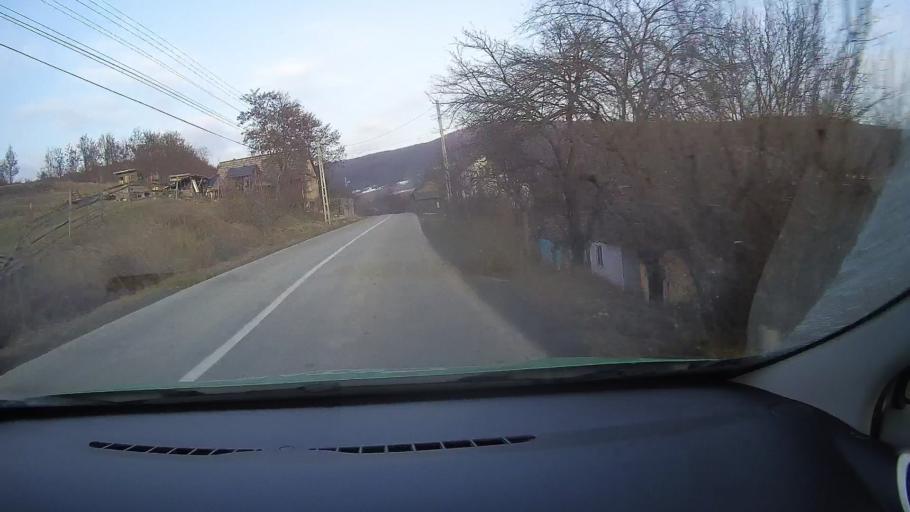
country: RO
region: Harghita
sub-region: Comuna Simonesti
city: Simonesti
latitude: 46.3070
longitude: 25.0779
